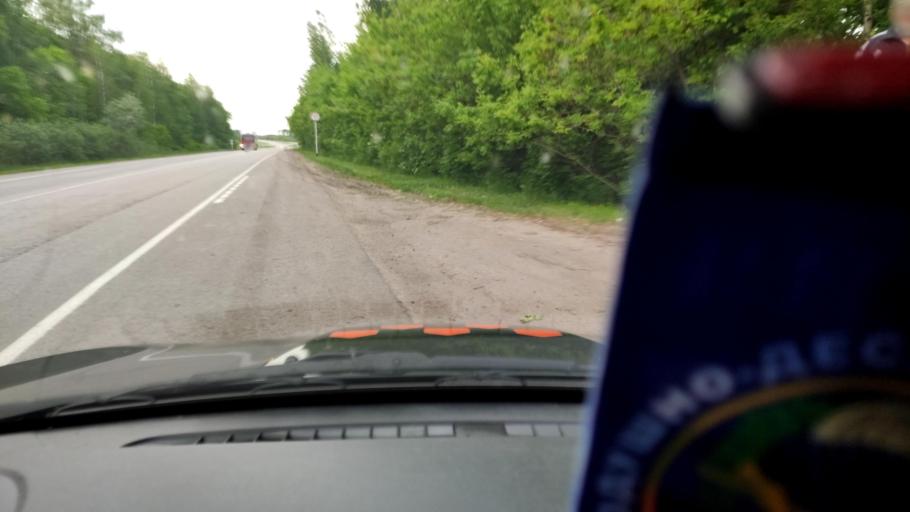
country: RU
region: Voronezj
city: Kolodeznyy
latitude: 51.3612
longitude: 39.0237
